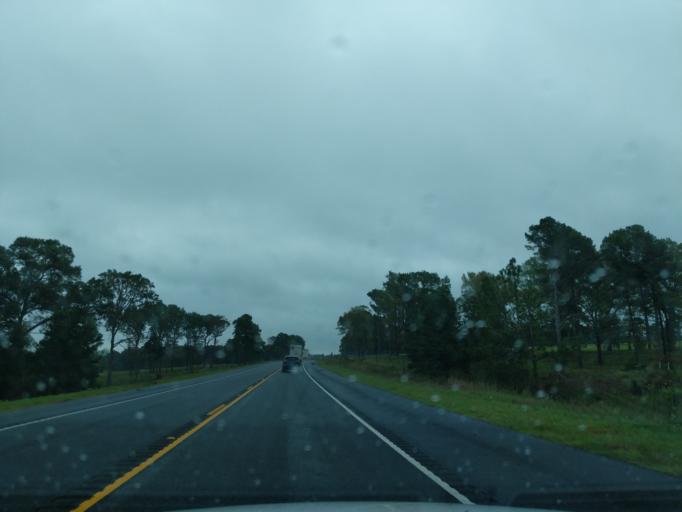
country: US
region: Louisiana
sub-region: Caddo Parish
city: Greenwood
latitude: 32.4342
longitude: -93.9840
